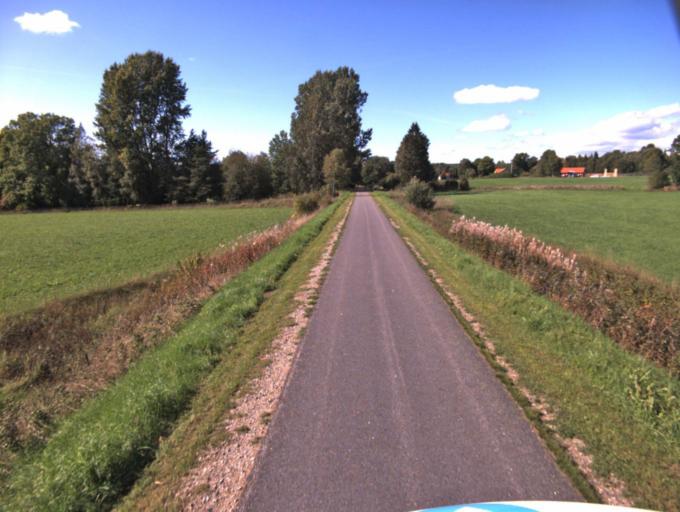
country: SE
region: Vaestra Goetaland
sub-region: Ulricehamns Kommun
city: Ulricehamn
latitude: 57.8007
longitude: 13.3764
